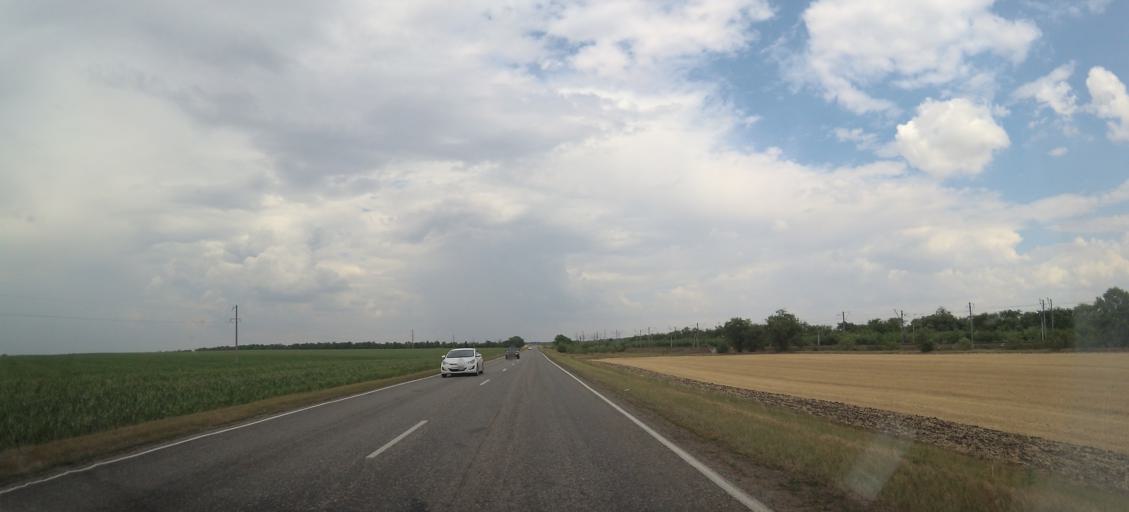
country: RU
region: Rostov
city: Krasnaya Polyana
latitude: 46.2621
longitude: 41.3624
